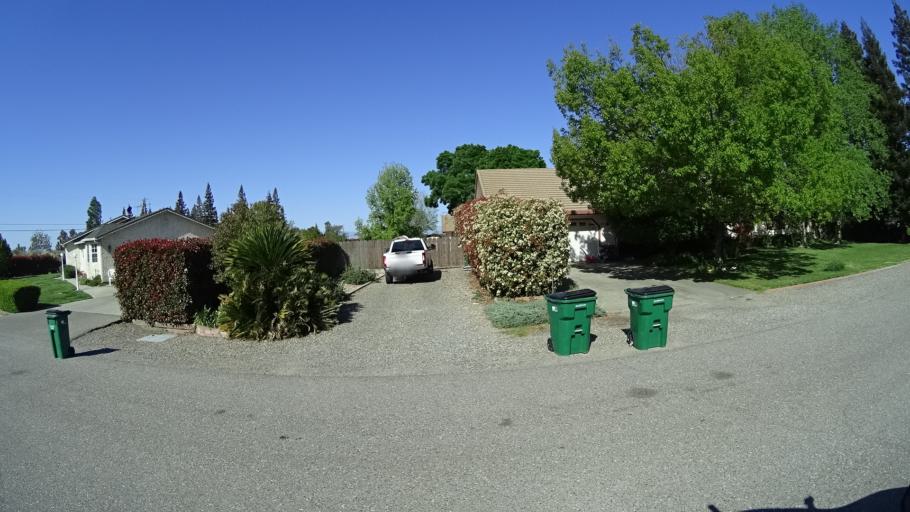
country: US
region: California
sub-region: Glenn County
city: Orland
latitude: 39.7294
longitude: -122.1655
